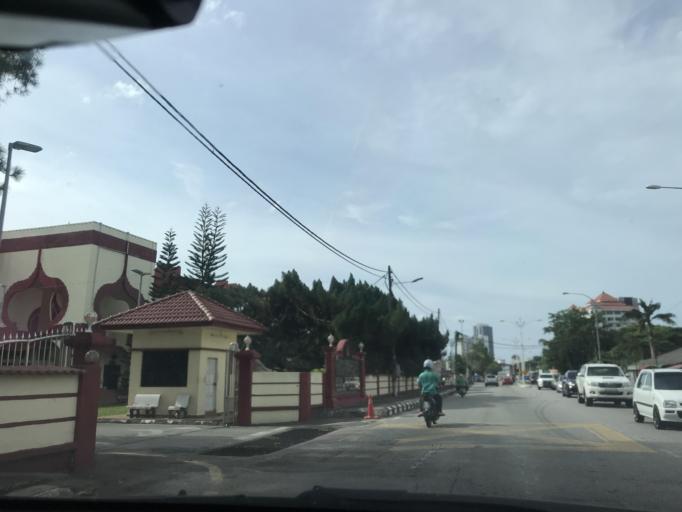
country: MY
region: Kelantan
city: Kota Bharu
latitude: 6.1081
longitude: 102.2366
